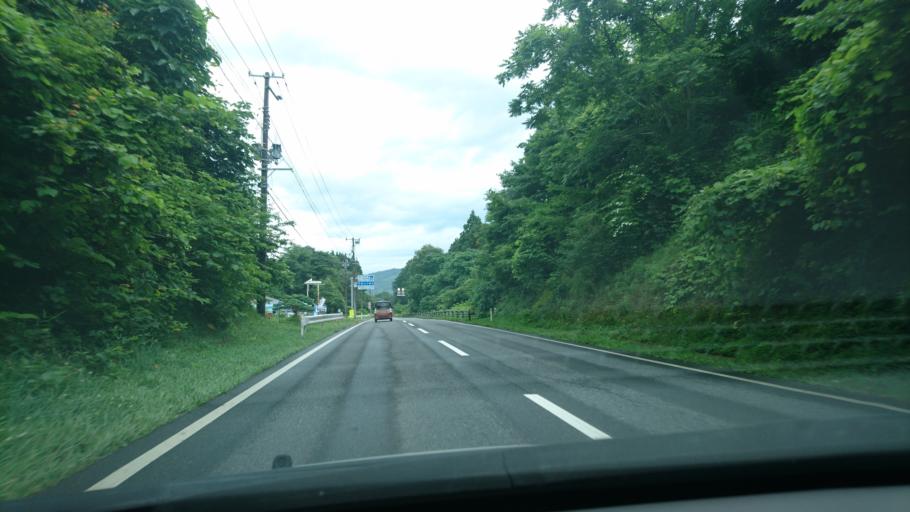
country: JP
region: Iwate
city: Yamada
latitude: 39.4178
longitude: 141.9686
